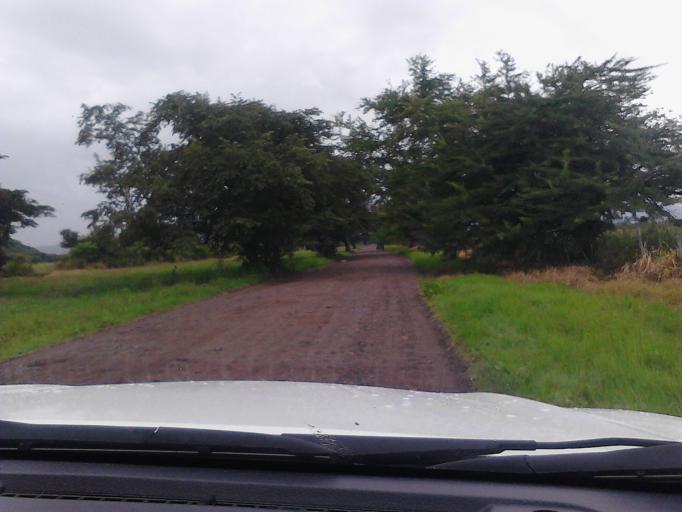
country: NI
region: Matagalpa
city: Ciudad Dario
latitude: 12.8940
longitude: -86.1533
